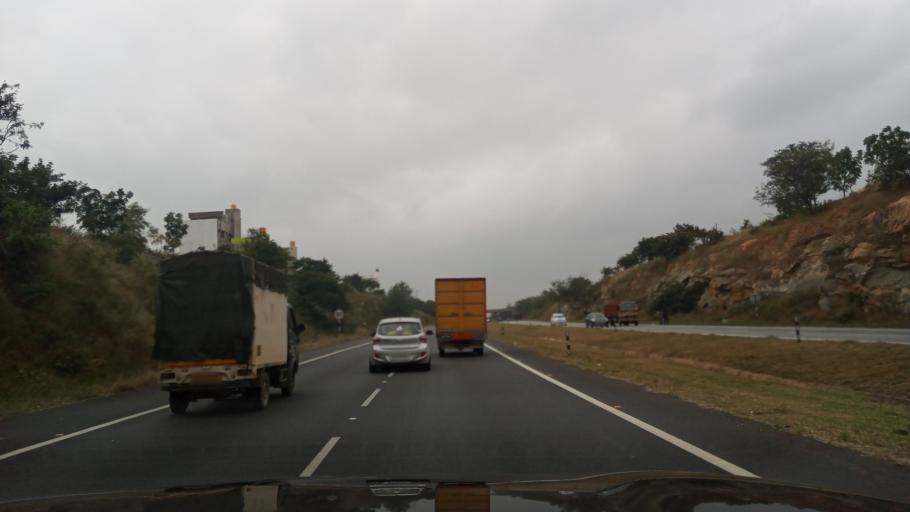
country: IN
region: Karnataka
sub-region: Bangalore Rural
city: Nelamangala
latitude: 13.0133
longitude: 77.4759
